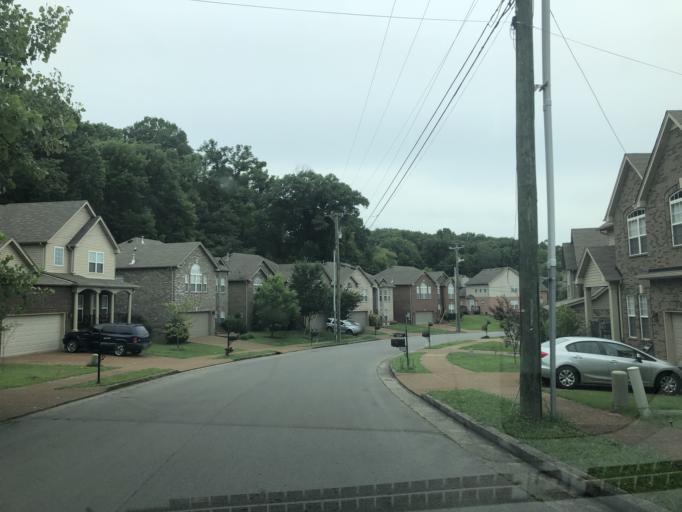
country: US
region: Tennessee
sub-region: Williamson County
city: Nolensville
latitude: 36.0305
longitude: -86.6797
